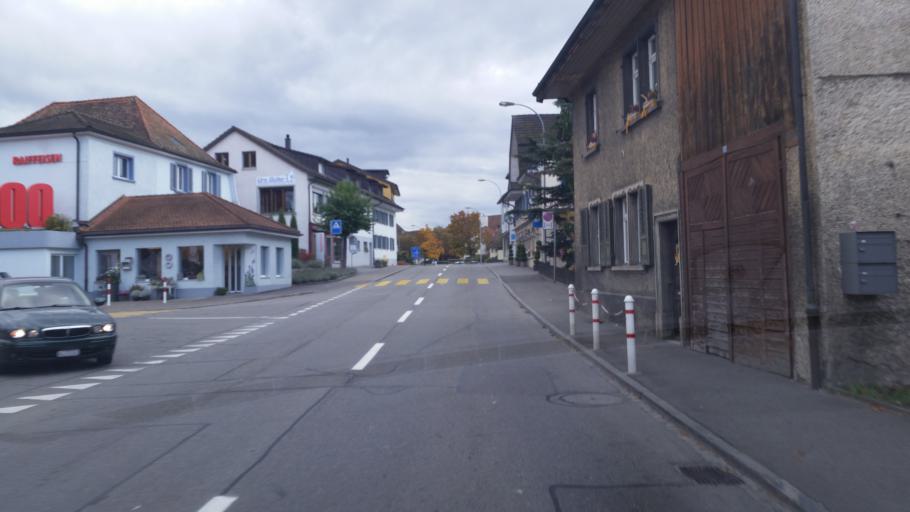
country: CH
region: Aargau
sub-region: Bezirk Zurzach
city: Klingnau
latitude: 47.5736
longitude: 8.2557
